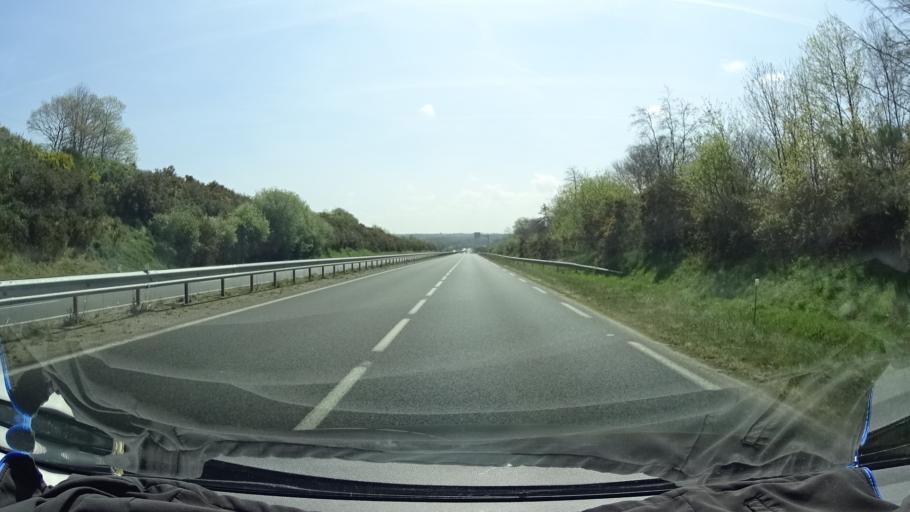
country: FR
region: Brittany
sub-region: Departement des Cotes-d'Armor
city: Plehedel
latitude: 48.6951
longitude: -3.0201
